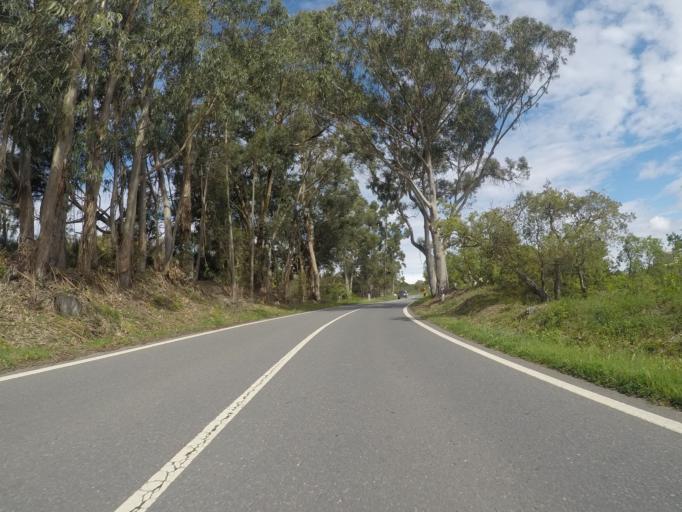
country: PT
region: Beja
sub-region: Odemira
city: Sao Teotonio
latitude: 37.4436
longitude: -8.7579
